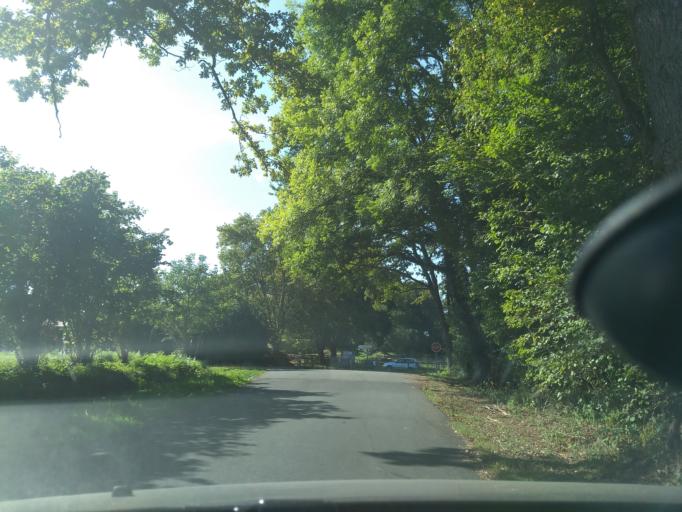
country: FR
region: Aquitaine
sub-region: Departement des Pyrenees-Atlantiques
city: Soumoulou
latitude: 43.2963
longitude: -0.1576
